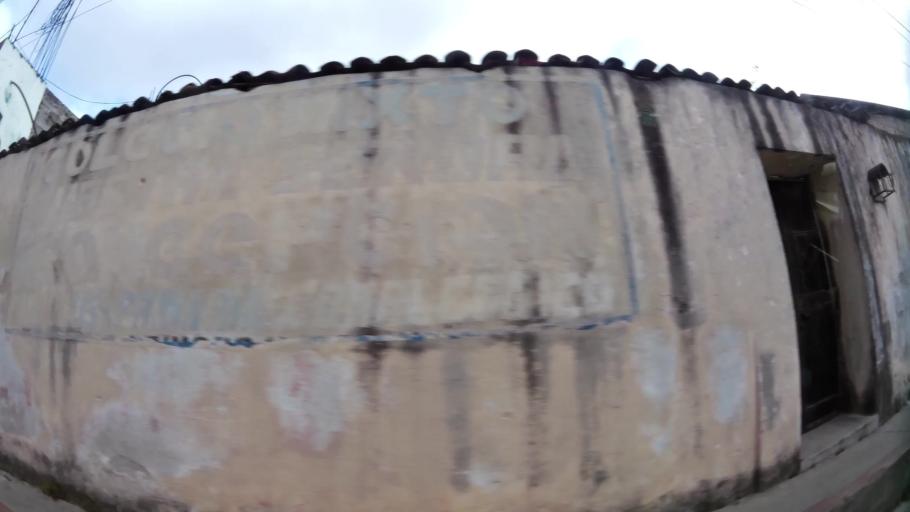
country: GT
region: Quetzaltenango
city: Salcaja
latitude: 14.8806
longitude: -91.4595
